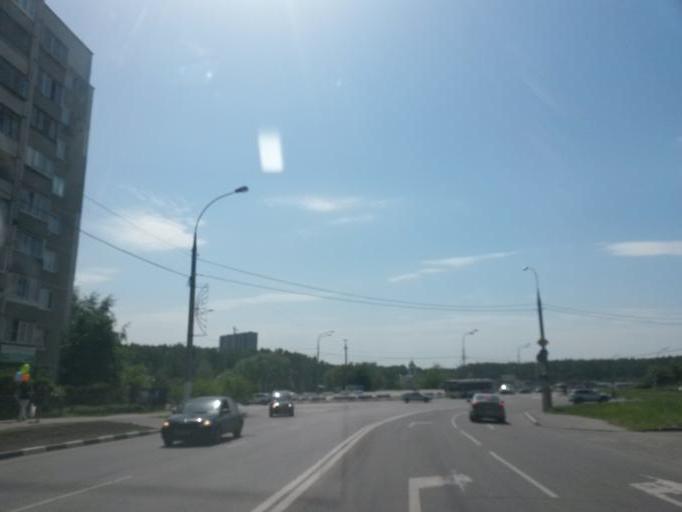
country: RU
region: Moscow
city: Chertanovo Yuzhnoye
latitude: 55.5669
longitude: 37.5608
